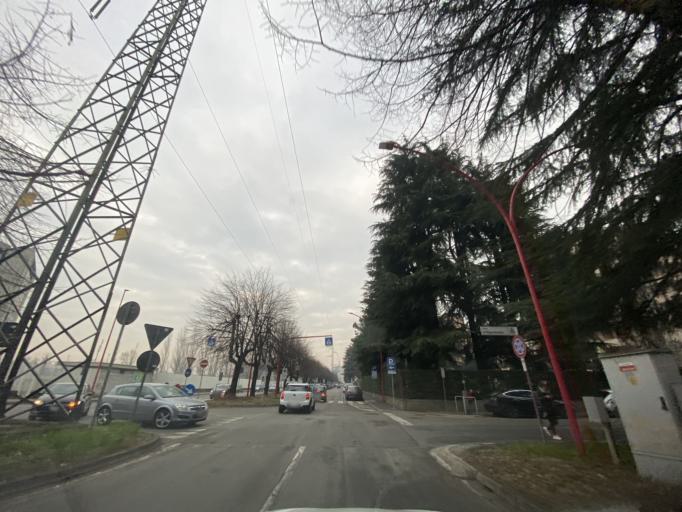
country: IT
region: Lombardy
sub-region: Citta metropolitana di Milano
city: Vimodrone
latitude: 45.5007
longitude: 9.2633
